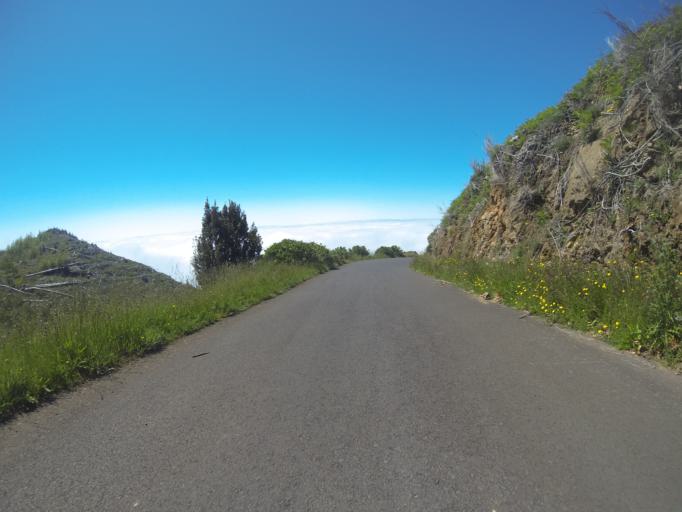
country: PT
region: Madeira
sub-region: Funchal
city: Nossa Senhora do Monte
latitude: 32.7032
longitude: -16.9138
